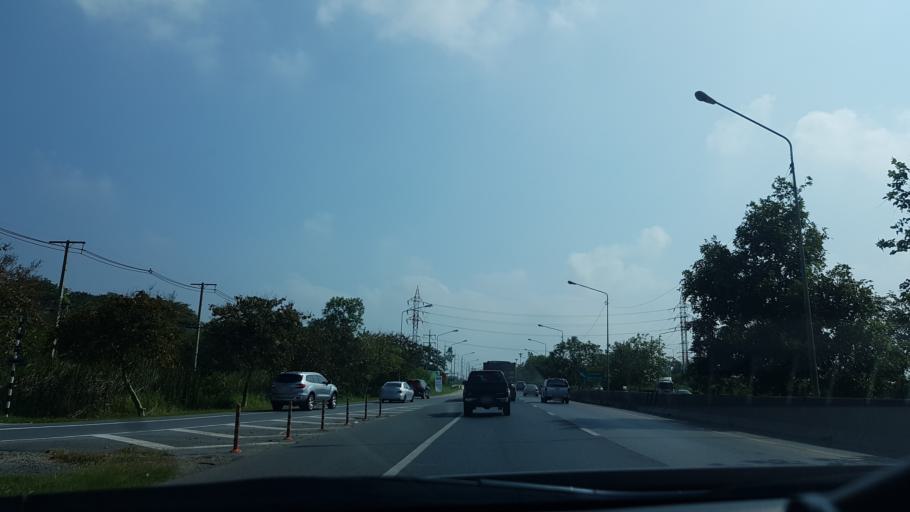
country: TH
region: Phra Nakhon Si Ayutthaya
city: Bang Pa-in
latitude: 14.1509
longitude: 100.5572
